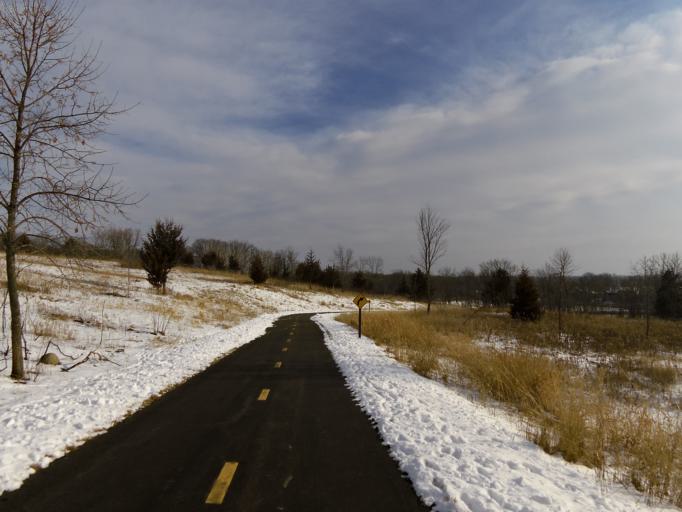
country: US
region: Minnesota
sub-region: Scott County
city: Prior Lake
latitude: 44.7091
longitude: -93.4728
